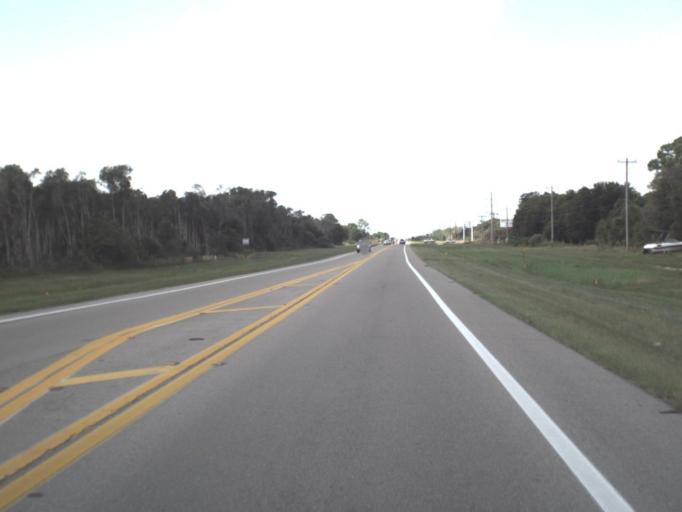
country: US
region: Florida
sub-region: Lee County
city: Lehigh Acres
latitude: 26.5577
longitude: -81.6581
